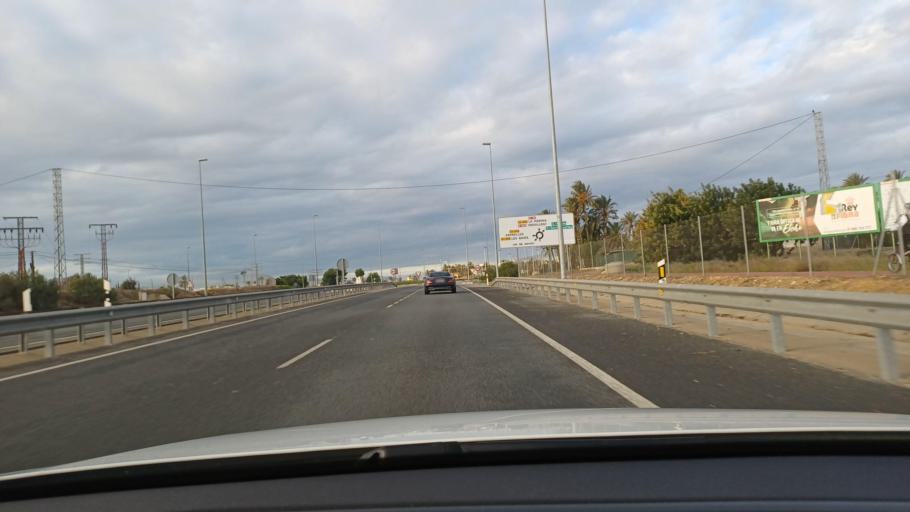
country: ES
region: Valencia
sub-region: Provincia de Alicante
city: Elche
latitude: 38.2568
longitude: -0.6842
